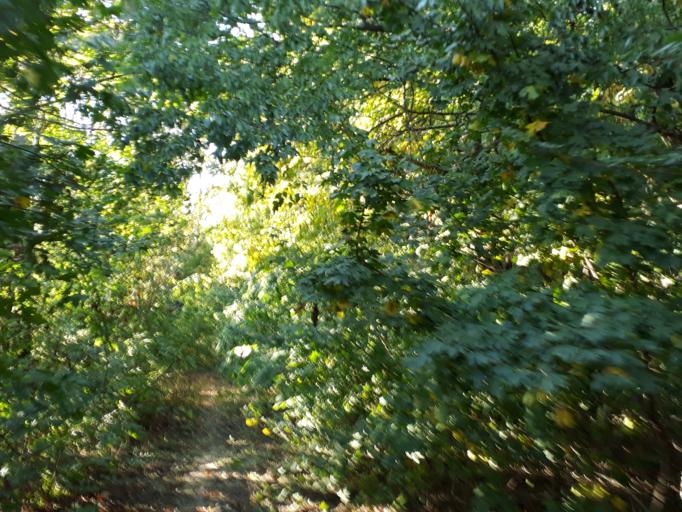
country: HU
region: Budapest
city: Budapest XII. keruelet
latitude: 47.4578
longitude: 19.0017
